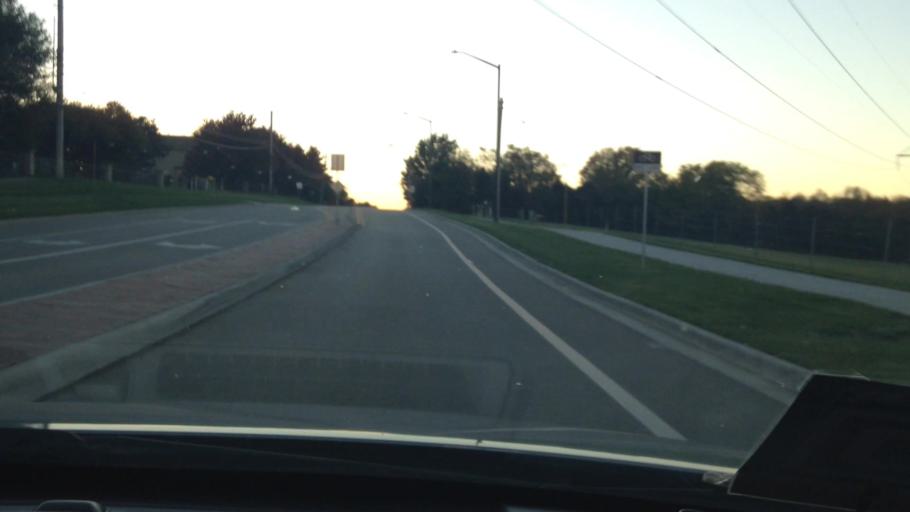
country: US
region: Kansas
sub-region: Johnson County
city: Olathe
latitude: 38.8692
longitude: -94.7426
